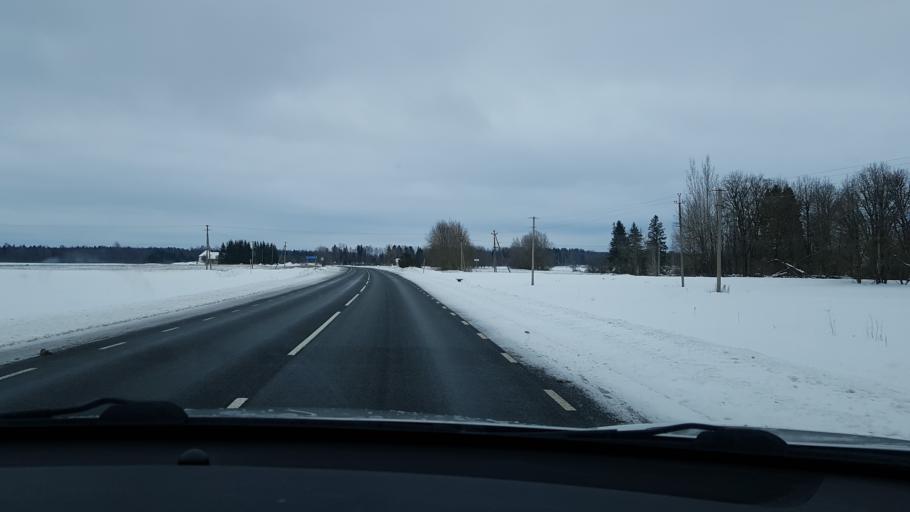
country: EE
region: Jaervamaa
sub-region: Jaerva-Jaani vald
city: Jarva-Jaani
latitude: 59.0844
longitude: 25.8390
